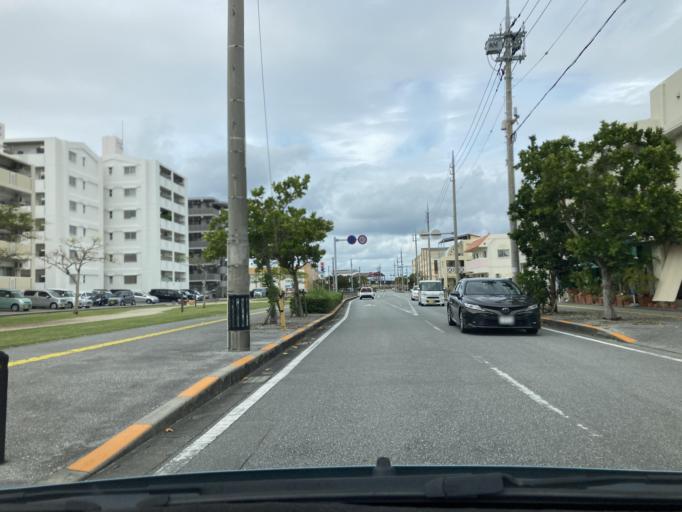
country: JP
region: Okinawa
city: Itoman
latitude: 26.1567
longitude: 127.6606
